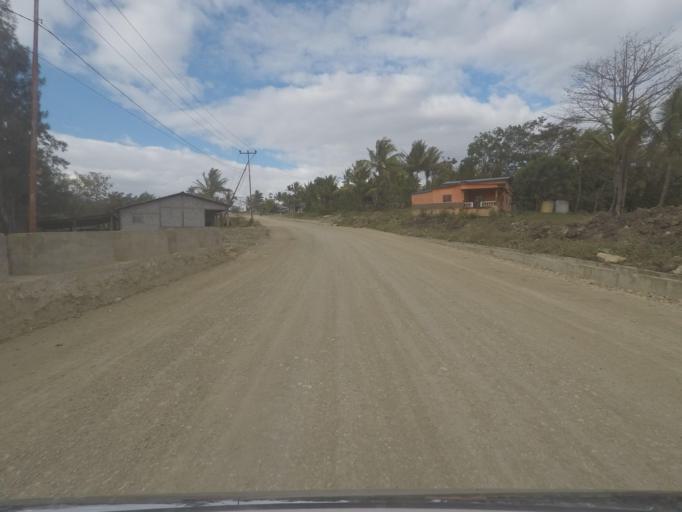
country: TL
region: Baucau
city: Venilale
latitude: -8.6384
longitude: 126.3772
